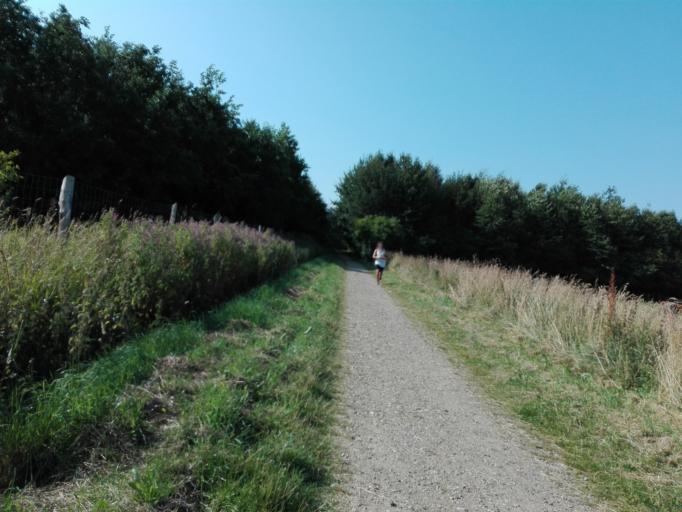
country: DK
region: Central Jutland
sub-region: Arhus Kommune
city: Arhus
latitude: 56.2028
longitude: 10.2047
